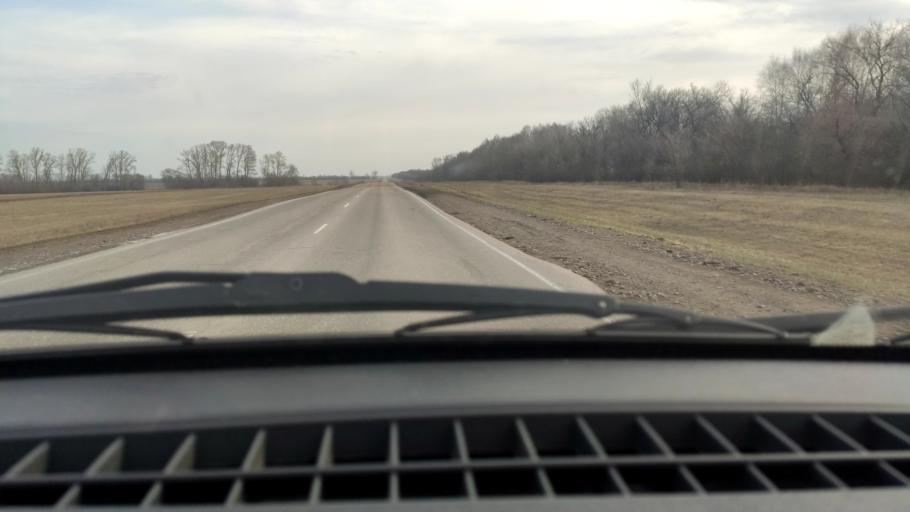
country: RU
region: Bashkortostan
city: Davlekanovo
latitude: 54.2545
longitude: 55.0843
